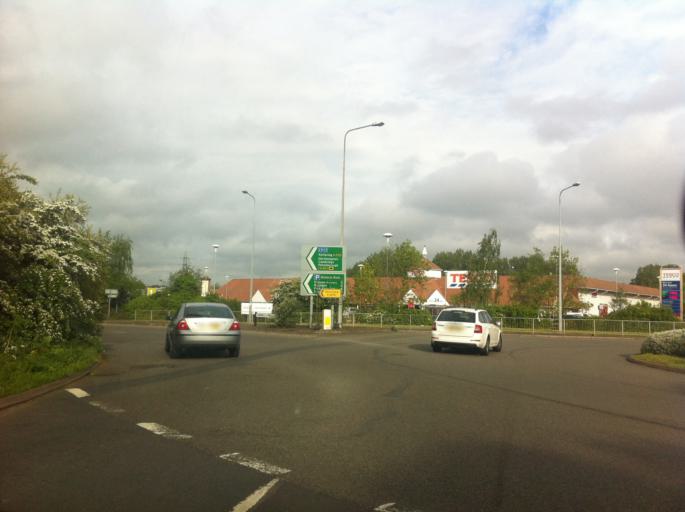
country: GB
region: England
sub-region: Northamptonshire
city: Wellingborough
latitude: 52.2901
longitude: -0.6819
